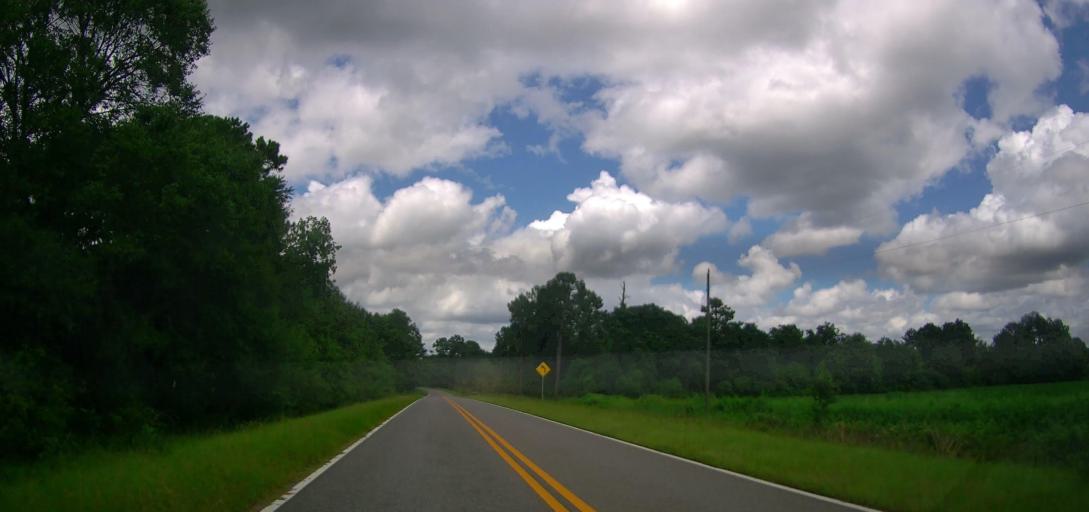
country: US
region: Georgia
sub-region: Turner County
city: Ashburn
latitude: 31.6890
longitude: -83.4762
